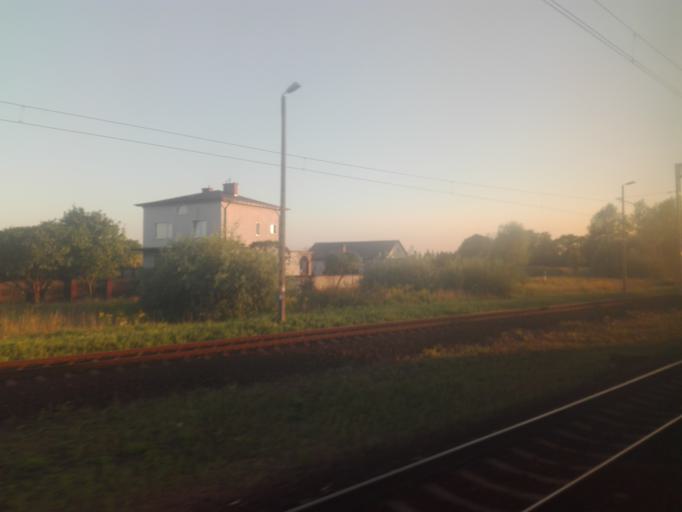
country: PL
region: Masovian Voivodeship
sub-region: Powiat warszawski zachodni
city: Blonie
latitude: 52.1865
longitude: 20.6041
